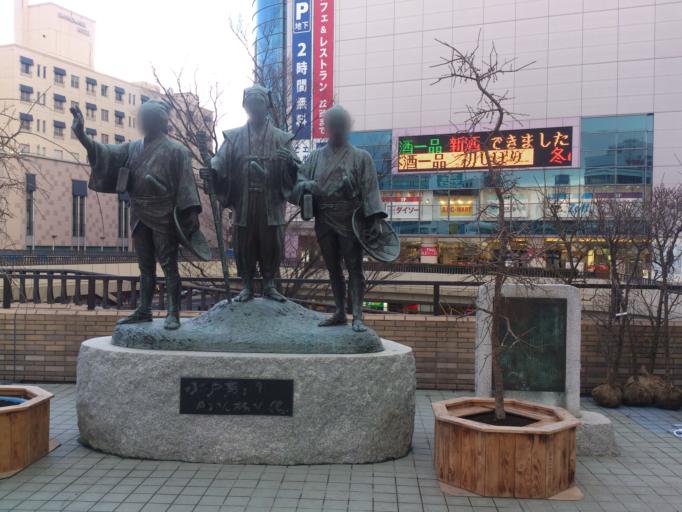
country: JP
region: Ibaraki
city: Mito-shi
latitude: 36.3717
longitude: 140.4763
